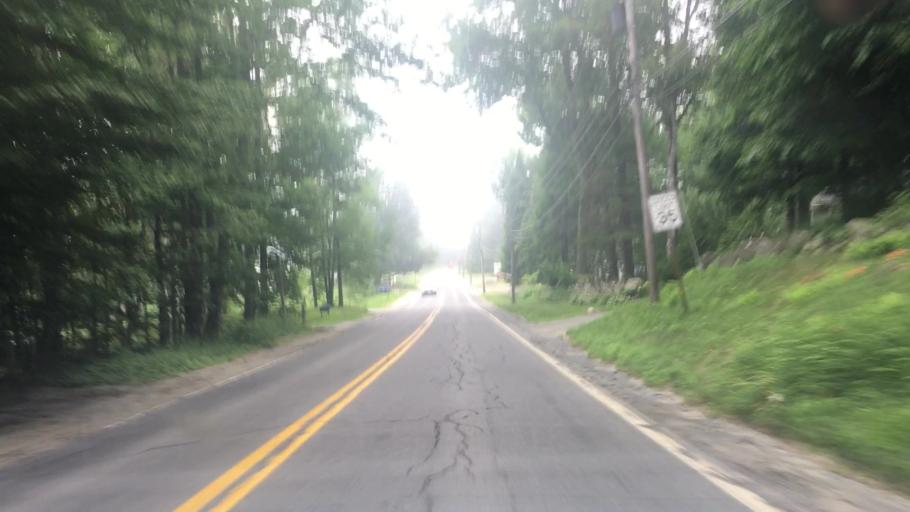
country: US
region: Maine
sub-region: Kennebec County
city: Oakland
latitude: 44.5327
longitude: -69.7237
